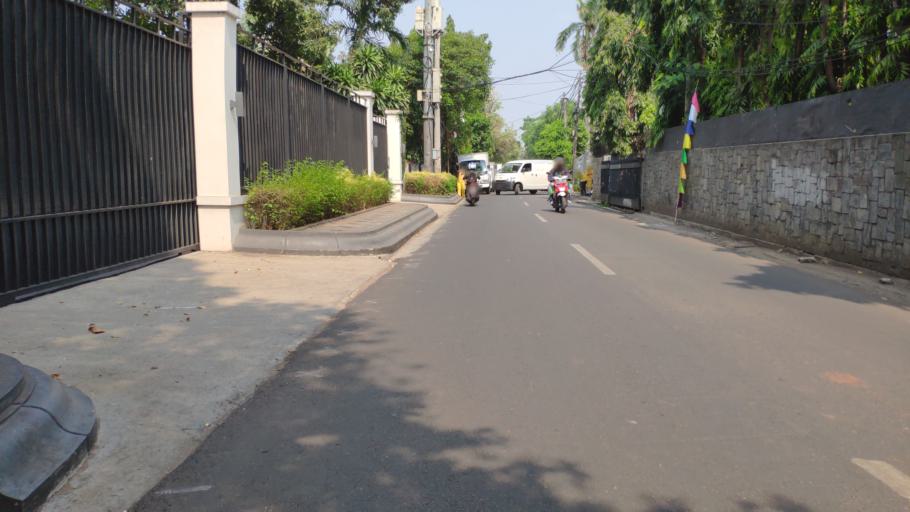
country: ID
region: Jakarta Raya
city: Jakarta
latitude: -6.2545
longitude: 106.8189
